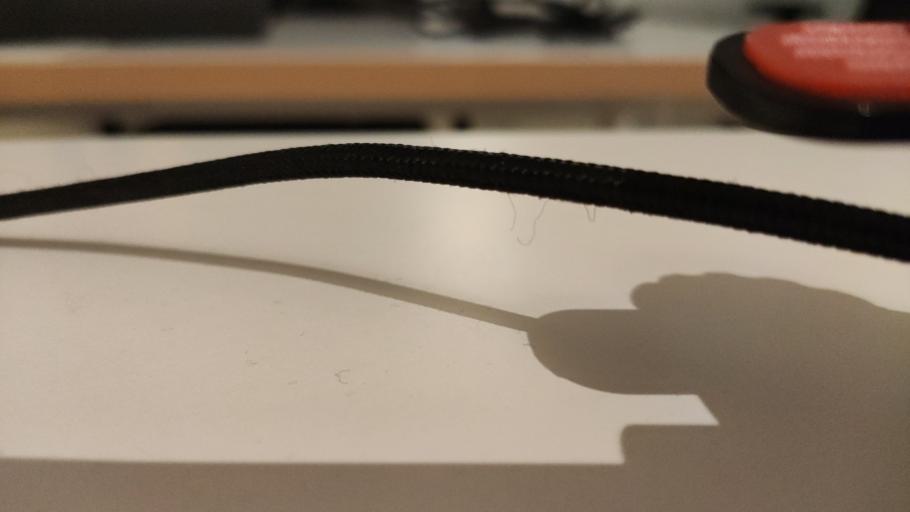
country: RU
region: Moskovskaya
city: Kurovskoye
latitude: 55.5375
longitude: 38.8728
